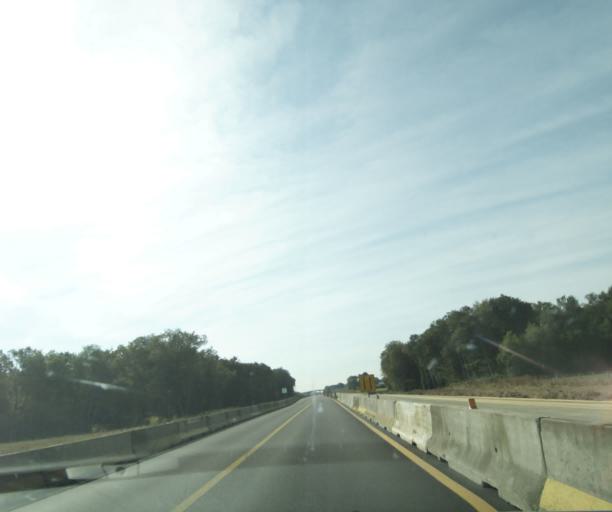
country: FR
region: Bourgogne
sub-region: Departement de Saone-et-Loire
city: Palinges
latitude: 46.5211
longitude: 4.1642
